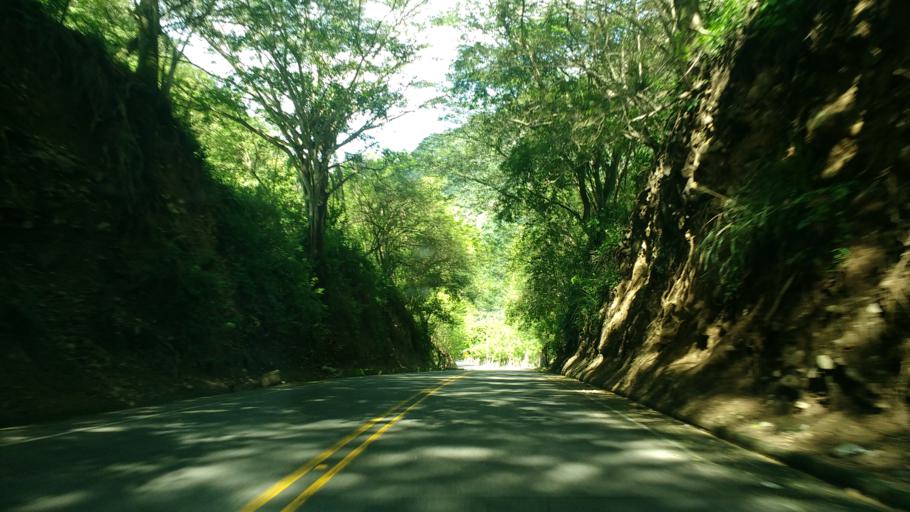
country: CO
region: Antioquia
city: Concordia
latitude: 6.0808
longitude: -75.8601
